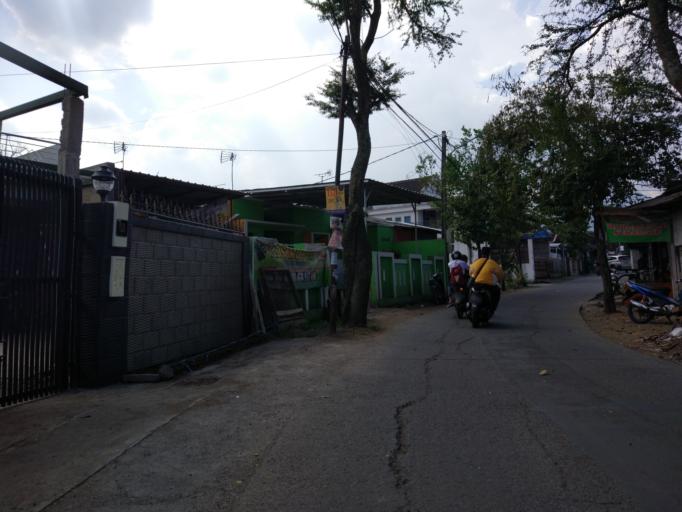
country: ID
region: West Java
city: Cileunyi
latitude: -6.9223
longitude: 107.7059
